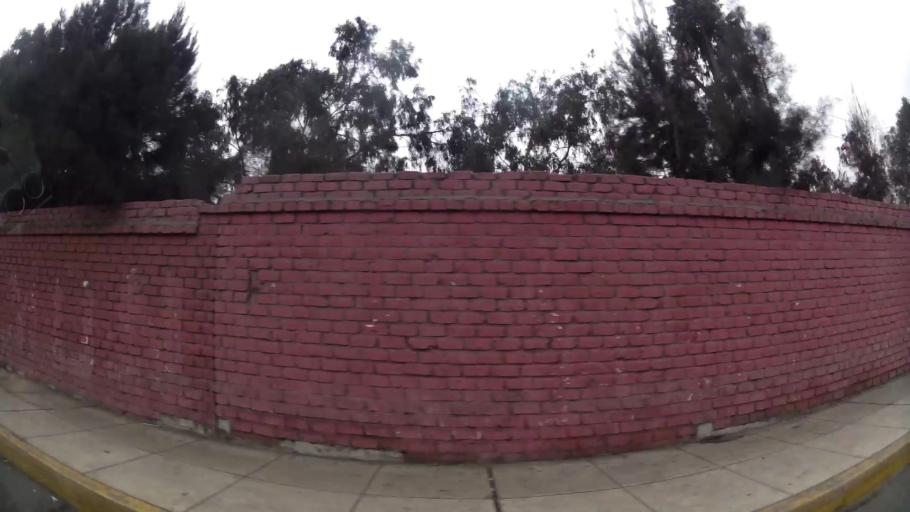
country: PE
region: Lima
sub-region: Lima
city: San Luis
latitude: -12.0982
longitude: -76.9751
